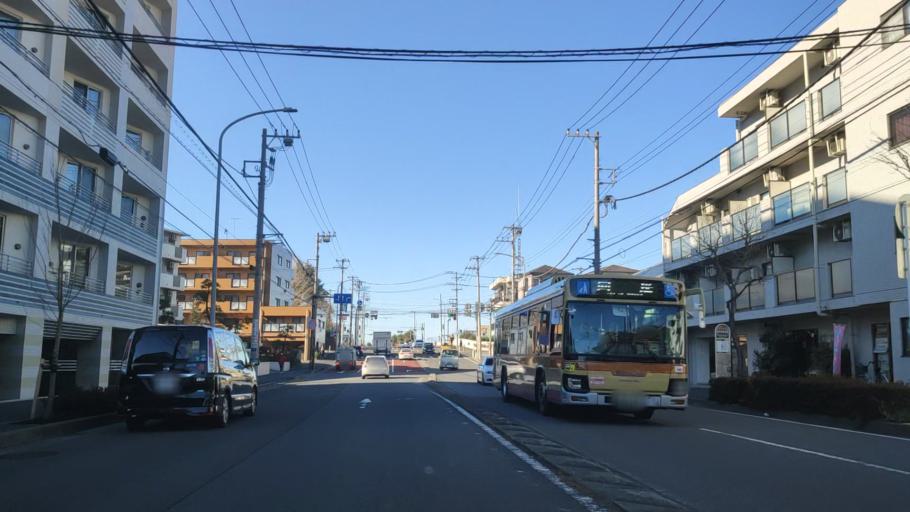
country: JP
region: Tokyo
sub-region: Machida-shi
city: Machida
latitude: 35.5159
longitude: 139.5352
